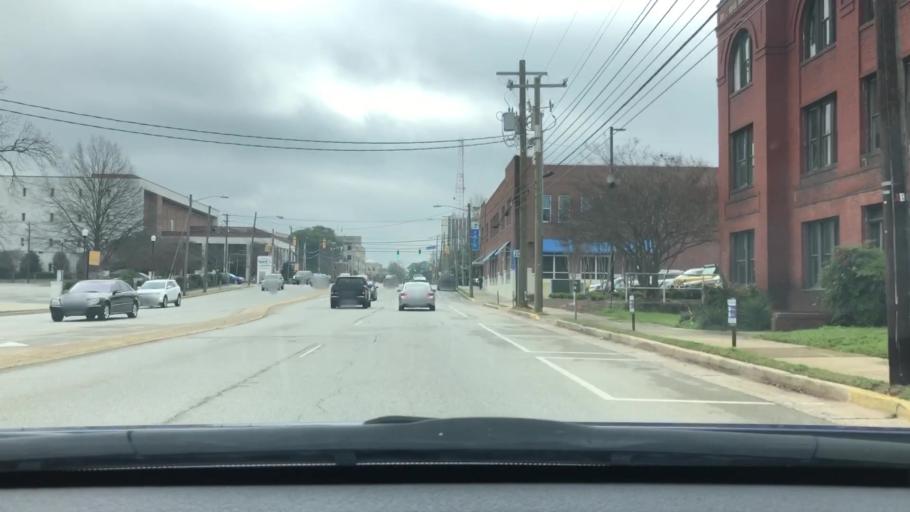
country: US
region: South Carolina
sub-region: Richland County
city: Columbia
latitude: 34.0077
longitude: -81.0310
